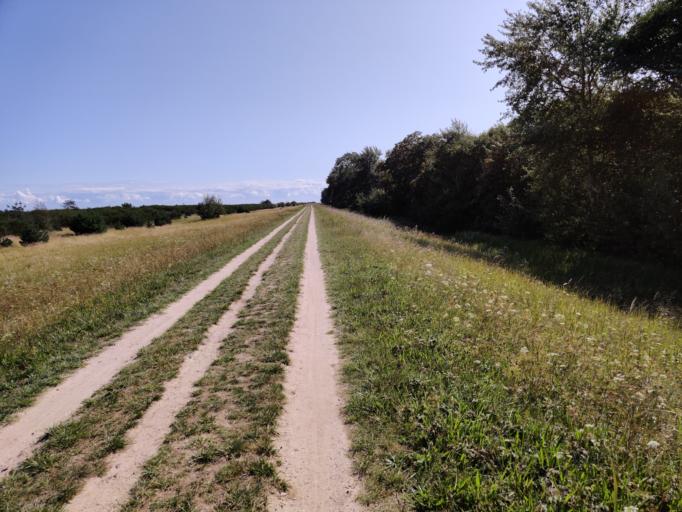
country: DK
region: Zealand
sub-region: Guldborgsund Kommune
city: Nykobing Falster
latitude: 54.6068
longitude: 11.9664
